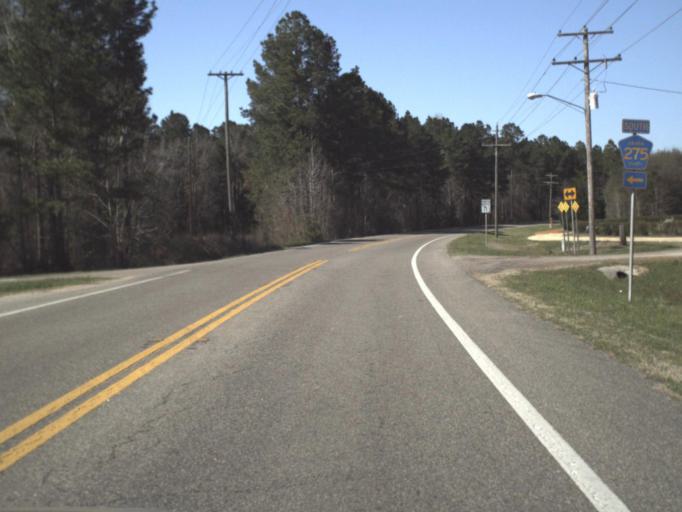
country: US
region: Florida
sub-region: Calhoun County
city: Blountstown
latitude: 30.5292
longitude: -85.1326
